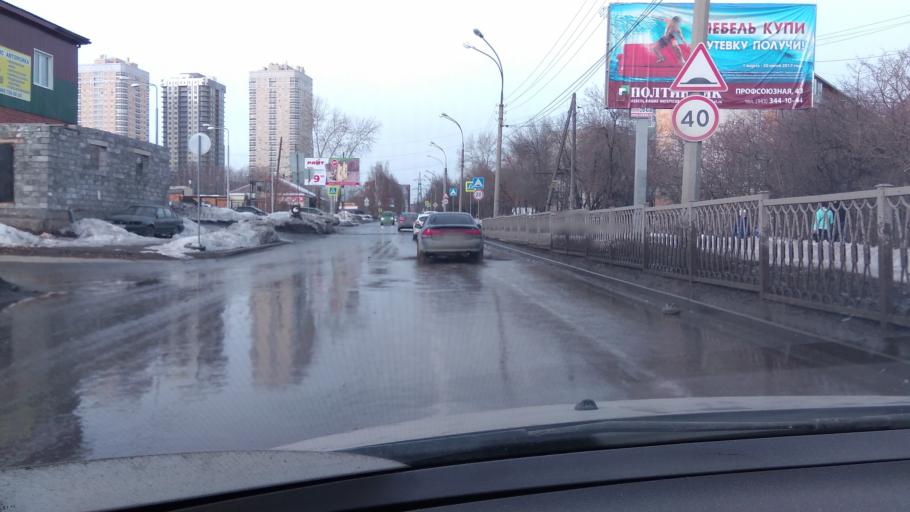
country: RU
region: Sverdlovsk
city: Sovkhoznyy
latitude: 56.7722
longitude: 60.6008
